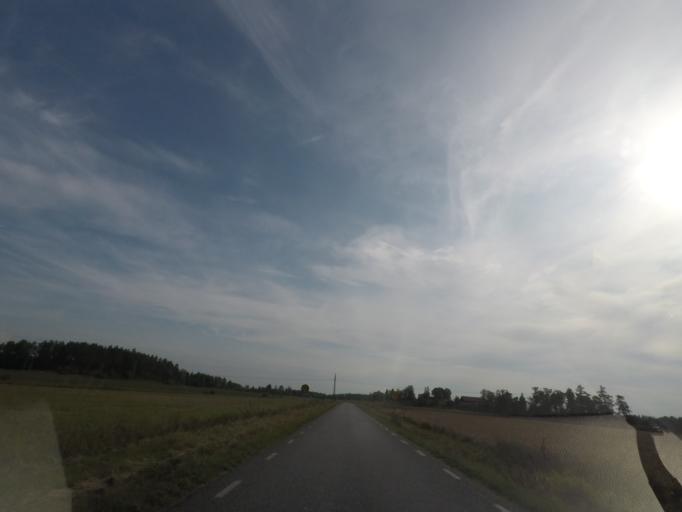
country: SE
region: Vaestmanland
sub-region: Hallstahammars Kommun
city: Kolback
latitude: 59.5316
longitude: 16.1415
